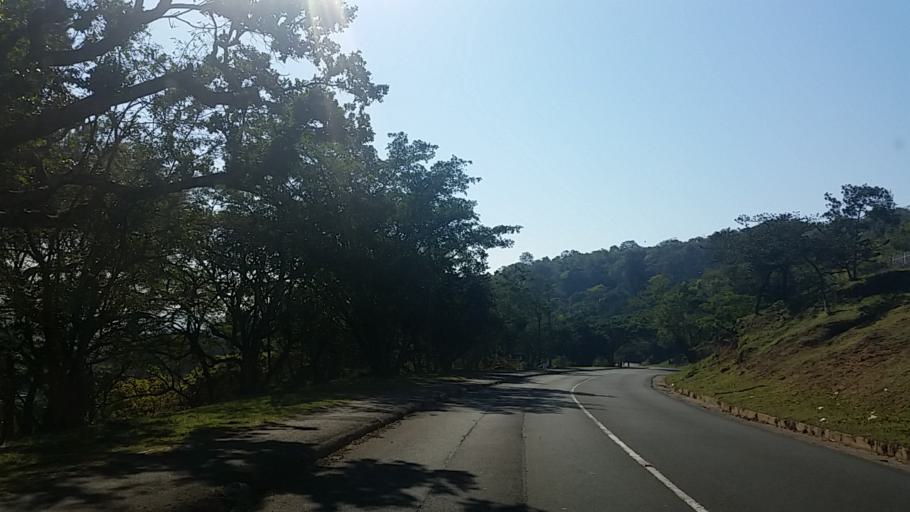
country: ZA
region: KwaZulu-Natal
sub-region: eThekwini Metropolitan Municipality
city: Berea
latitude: -29.8277
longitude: 30.8854
